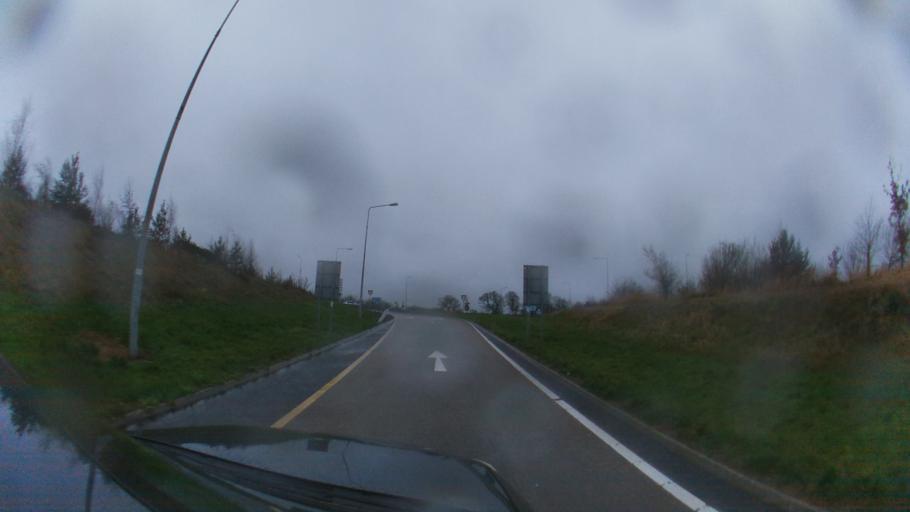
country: IE
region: Leinster
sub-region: County Carlow
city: Bagenalstown
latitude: 52.6808
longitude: -7.0379
